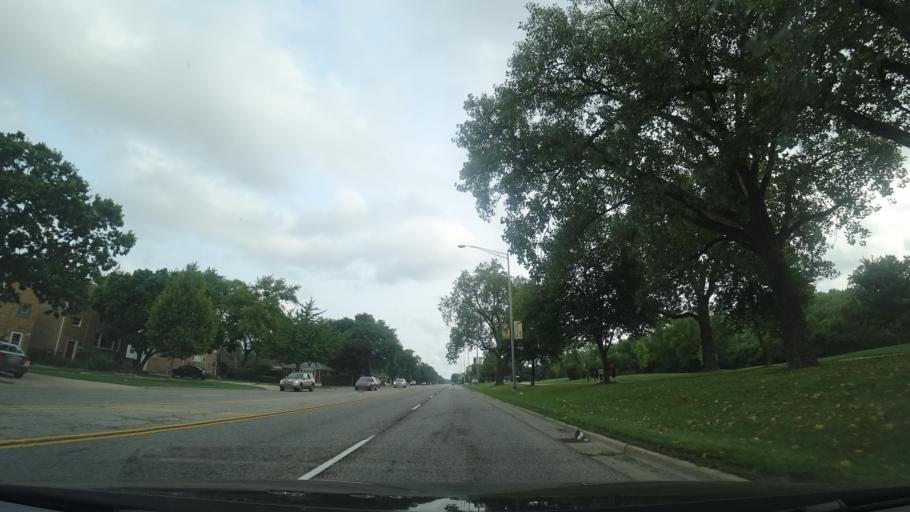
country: US
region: Illinois
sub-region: Cook County
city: Evanston
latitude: 42.0366
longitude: -87.7108
